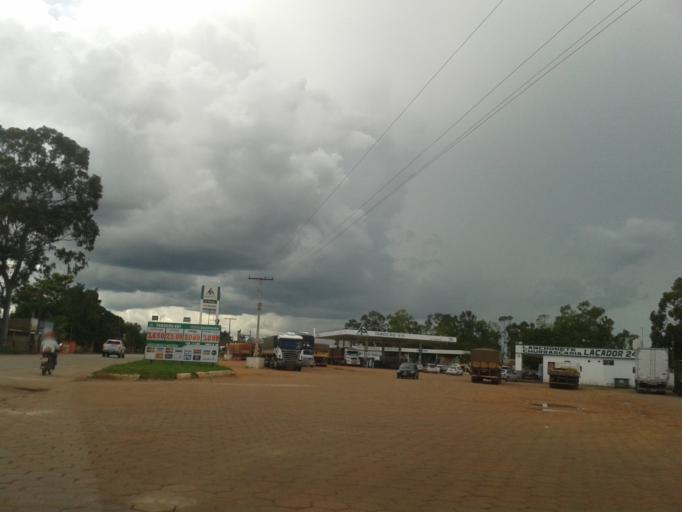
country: BR
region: Goias
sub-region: Itaberai
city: Itaberai
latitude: -16.0470
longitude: -49.7892
